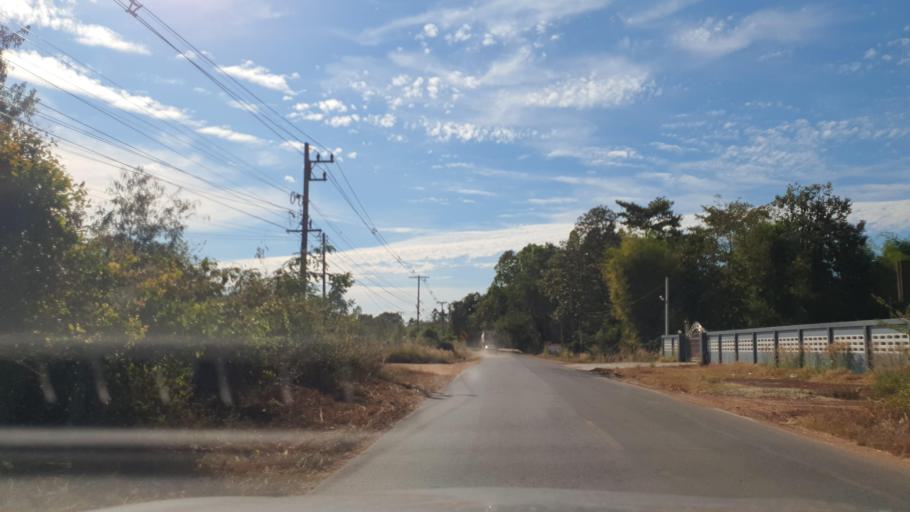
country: TH
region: Kalasin
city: Kuchinarai
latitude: 16.5408
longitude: 104.0821
